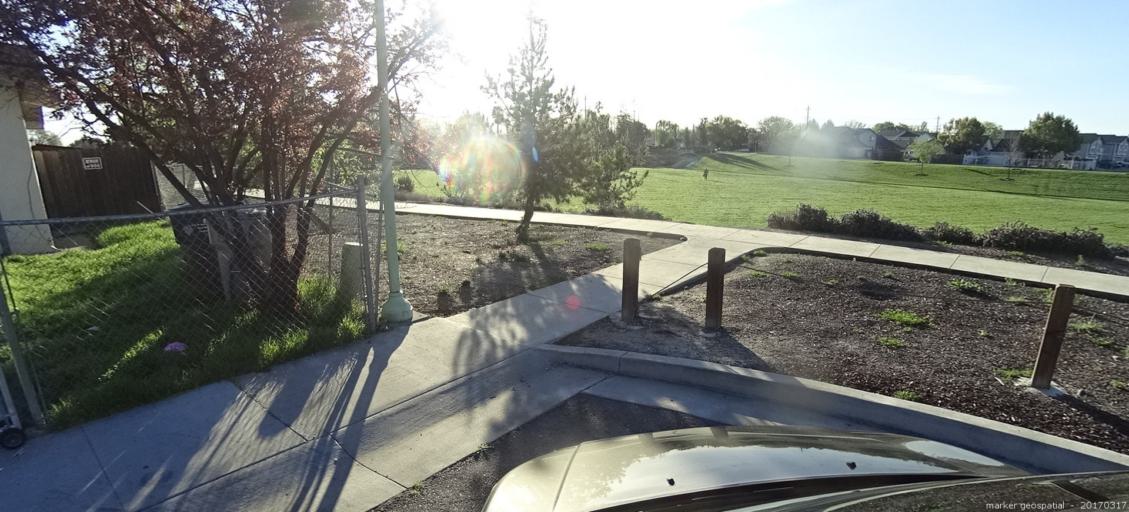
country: US
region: California
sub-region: Sacramento County
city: Parkway
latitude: 38.4854
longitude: -121.4819
